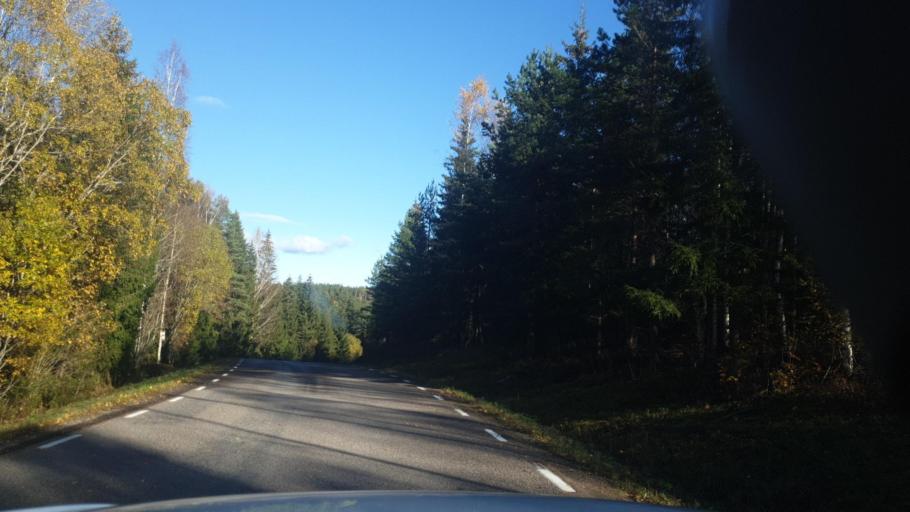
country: SE
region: Vaermland
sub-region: Arvika Kommun
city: Arvika
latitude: 59.6080
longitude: 12.7720
